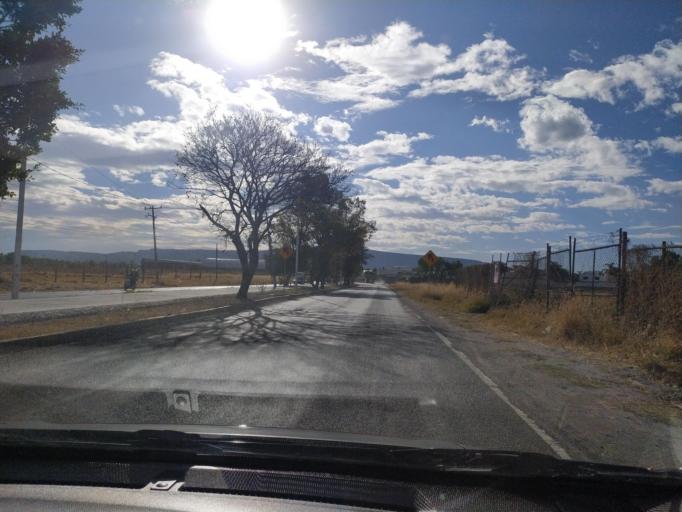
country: LA
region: Oudomxai
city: Muang La
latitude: 21.0321
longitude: 101.8397
